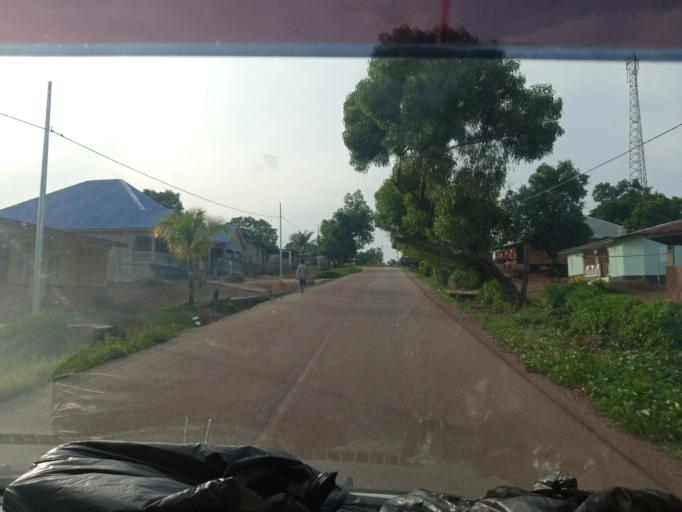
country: SL
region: Southern Province
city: Largo
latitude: 8.1990
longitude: -12.0591
